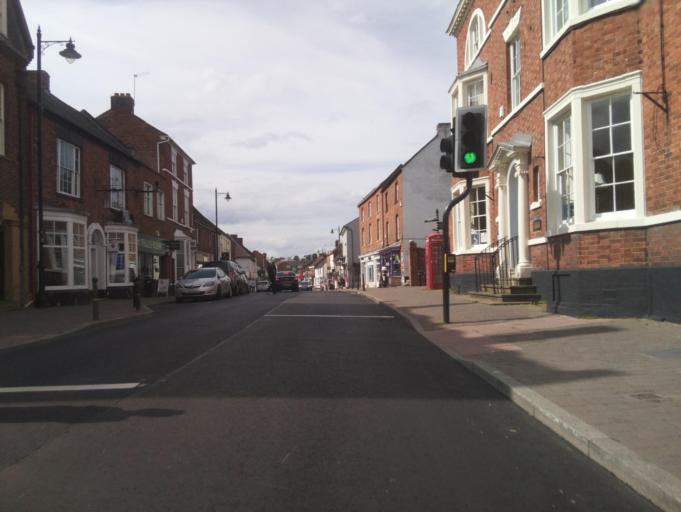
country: GB
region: England
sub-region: Worcestershire
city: Pershore
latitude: 52.1111
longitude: -2.0754
